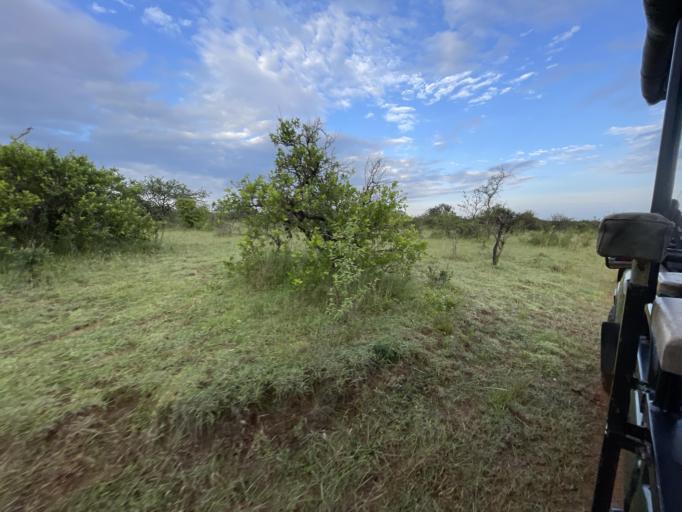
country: TZ
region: Mara
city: Mugumu
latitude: -1.7025
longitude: 35.3070
